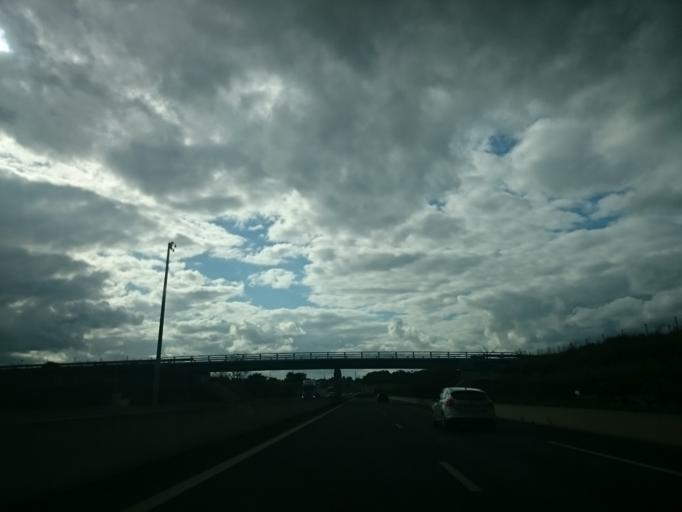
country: FR
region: Brittany
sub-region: Departement d'Ille-et-Vilaine
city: Vezin-le-Coquet
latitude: 48.1258
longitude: -1.7245
